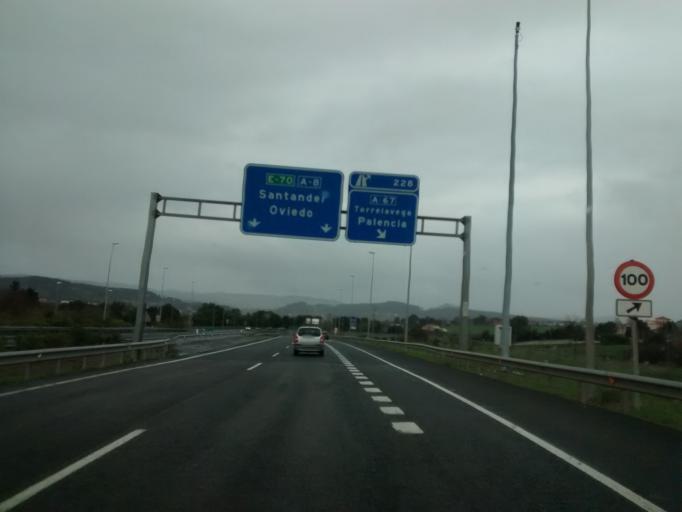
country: ES
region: Cantabria
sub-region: Provincia de Cantabria
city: Torrelavega
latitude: 43.3471
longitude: -4.0281
